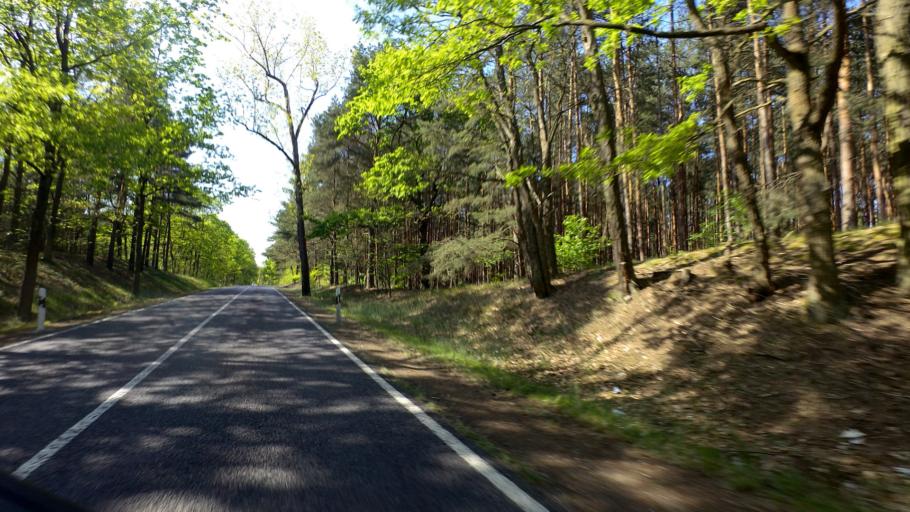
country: DE
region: Brandenburg
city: Munchehofe
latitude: 52.0973
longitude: 13.8349
